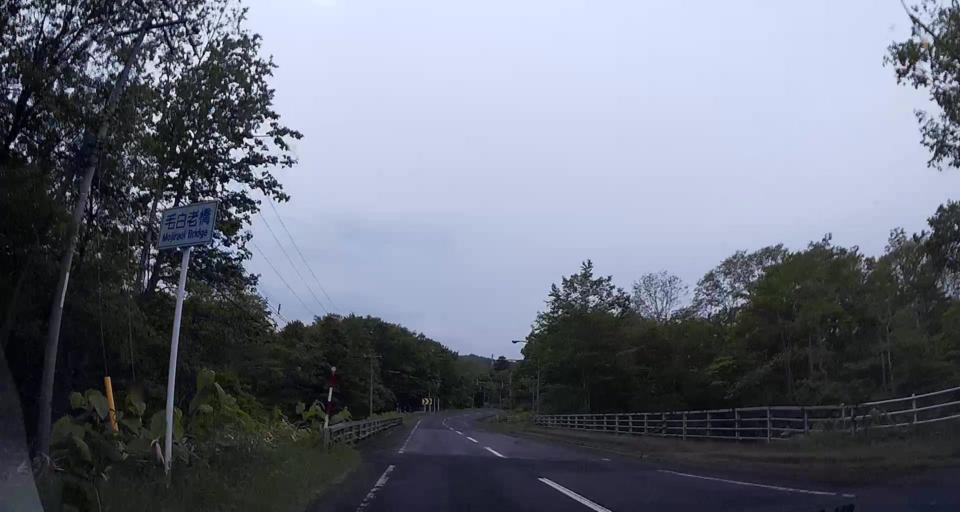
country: JP
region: Hokkaido
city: Shiraoi
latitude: 42.6075
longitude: 141.2854
